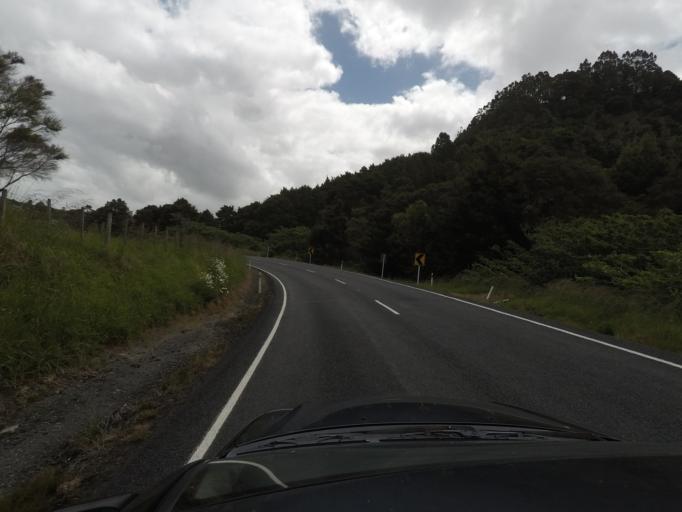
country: NZ
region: Auckland
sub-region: Auckland
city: Parakai
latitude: -36.5019
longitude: 174.5231
